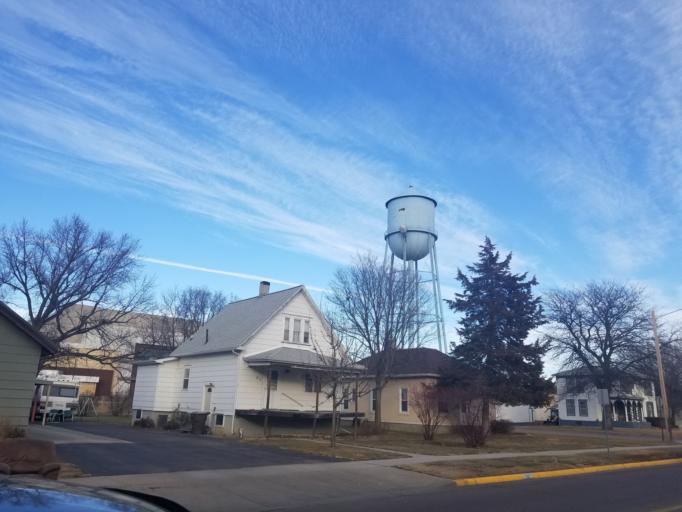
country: US
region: South Dakota
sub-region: Davison County
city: Mitchell
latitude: 43.7156
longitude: -98.0189
